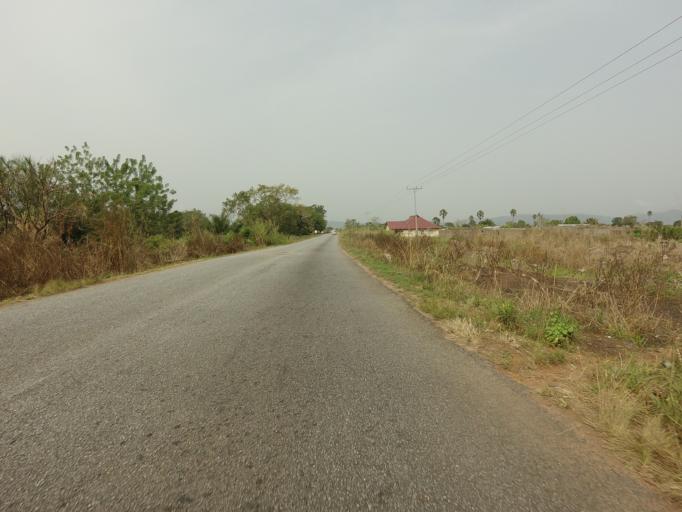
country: GH
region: Volta
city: Ho
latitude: 6.5727
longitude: 0.3629
